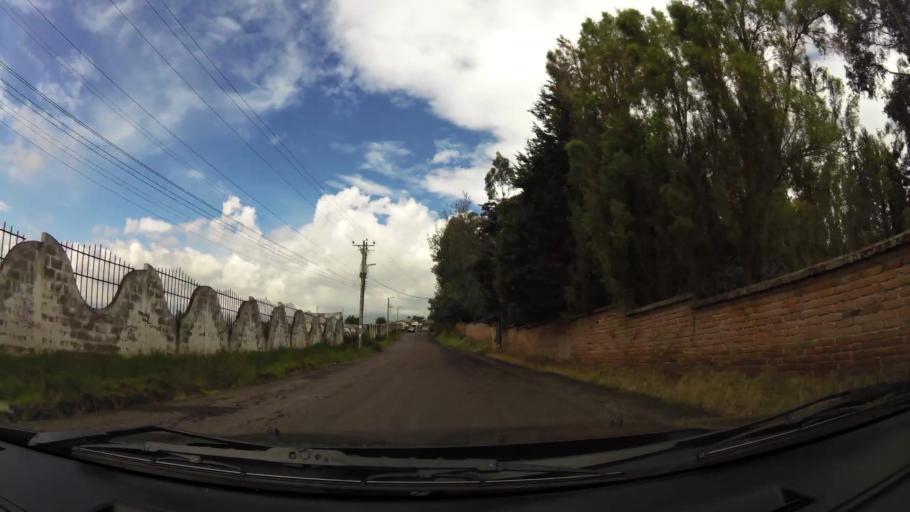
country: EC
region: Pichincha
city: Sangolqui
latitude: -0.3165
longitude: -78.4034
